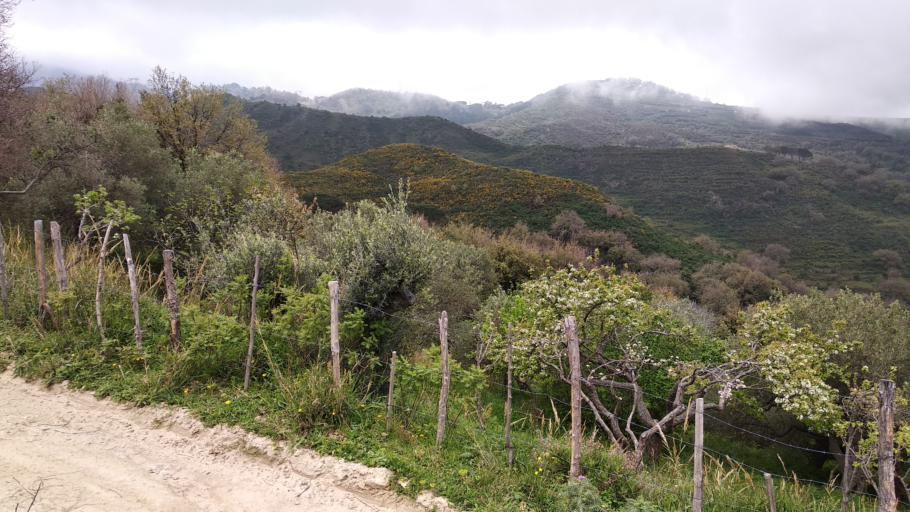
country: IT
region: Sicily
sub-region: Messina
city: Villafranca Tirrena
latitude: 38.2157
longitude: 15.4736
